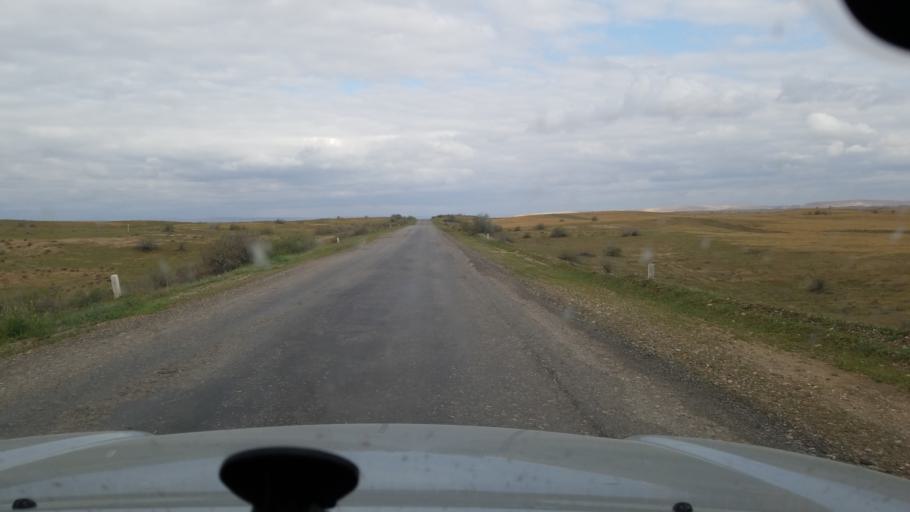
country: TM
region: Mary
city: Serhetabat
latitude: 35.9847
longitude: 62.6310
